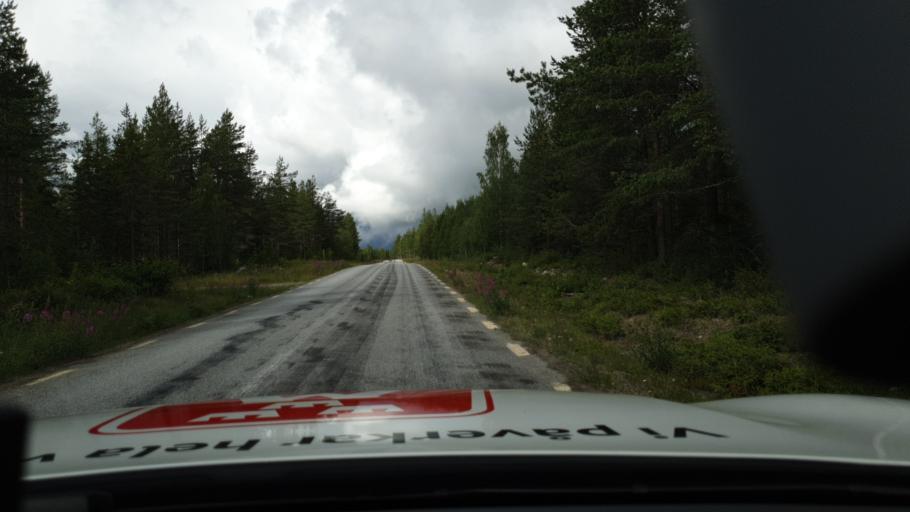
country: SE
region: Norrbotten
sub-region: Pitea Kommun
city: Rosvik
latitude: 65.4213
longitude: 21.8243
